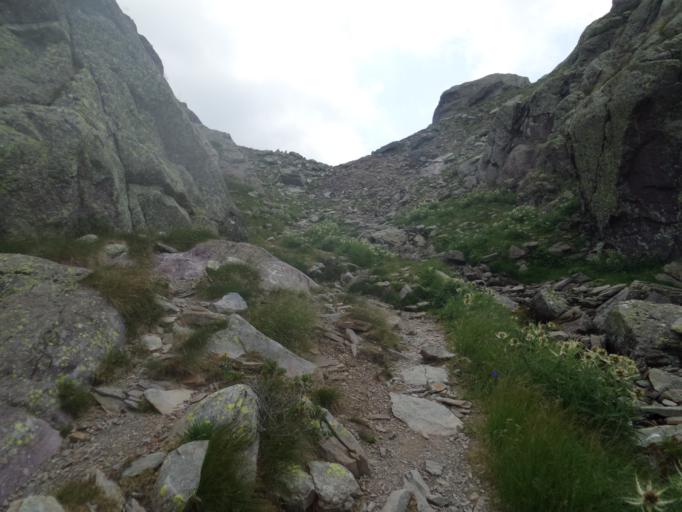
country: IT
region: Lombardy
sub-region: Provincia di Sondrio
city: Gerola Alta
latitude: 46.0273
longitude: 9.5211
